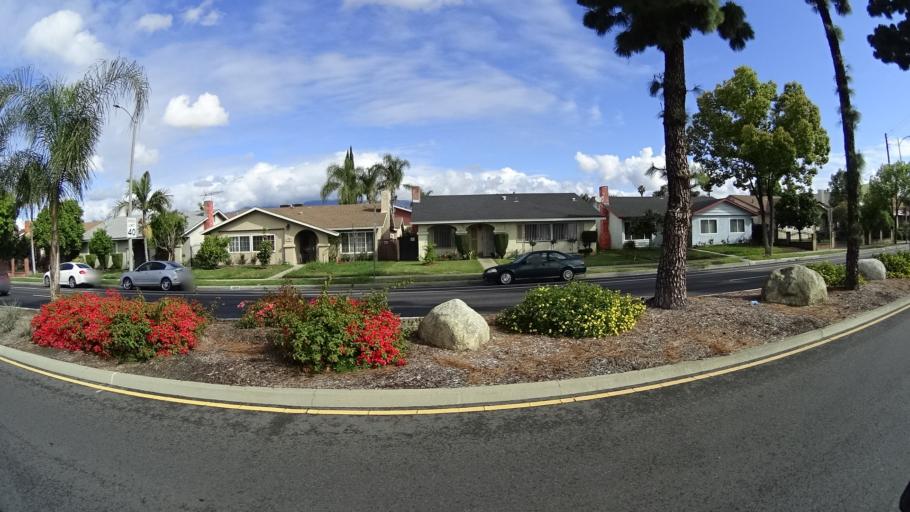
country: US
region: California
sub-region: Los Angeles County
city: Baldwin Park
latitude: 34.0872
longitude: -117.9458
